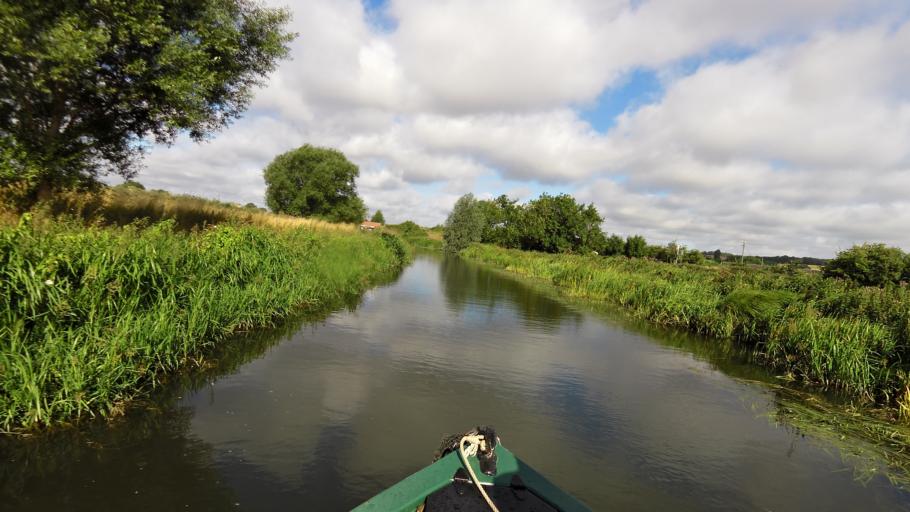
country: GB
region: England
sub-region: West Berkshire
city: Thatcham
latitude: 51.3925
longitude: -1.2069
